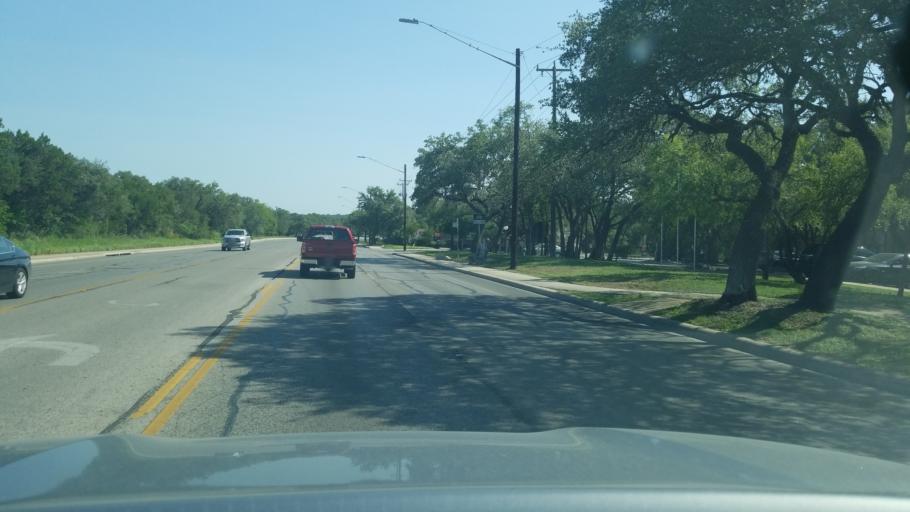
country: US
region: Texas
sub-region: Bexar County
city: Hollywood Park
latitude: 29.5937
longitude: -98.5115
